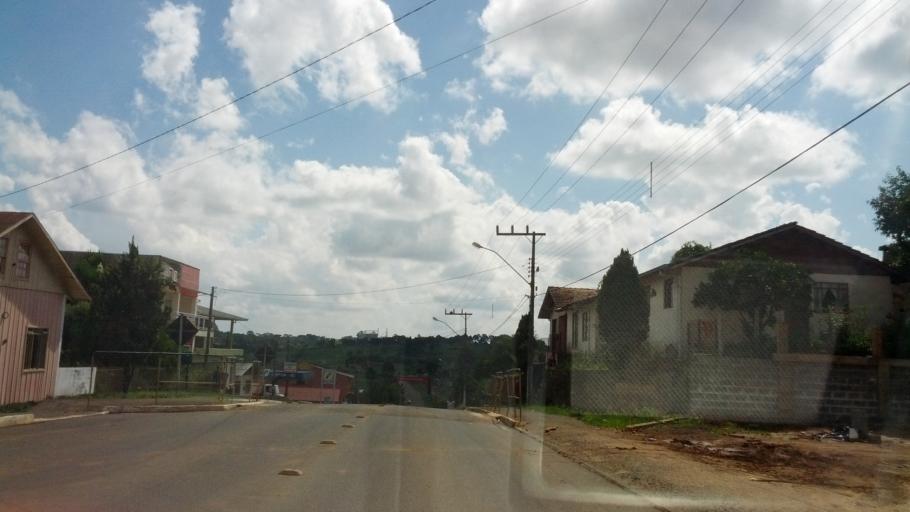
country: BR
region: Rio Grande do Sul
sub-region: Vacaria
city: Estrela
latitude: -27.7976
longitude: -50.8743
